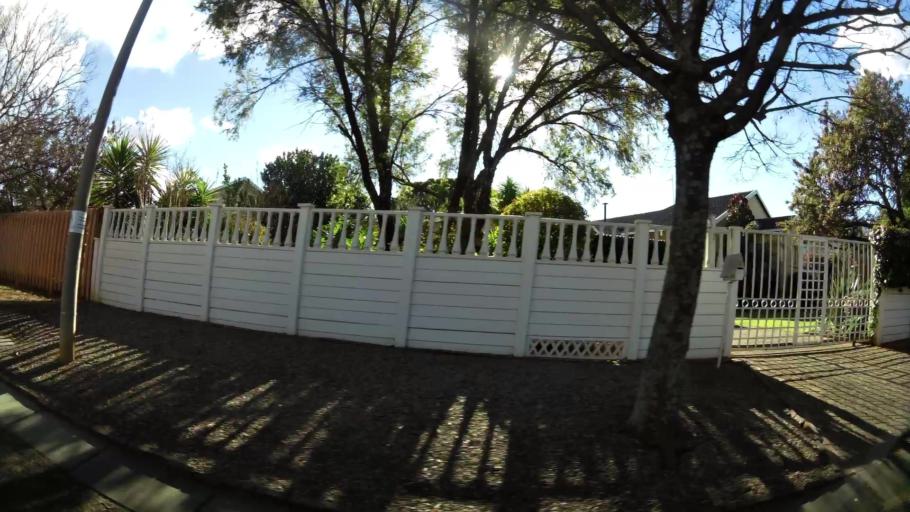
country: ZA
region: North-West
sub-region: Dr Kenneth Kaunda District Municipality
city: Klerksdorp
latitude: -26.8254
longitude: 26.6773
